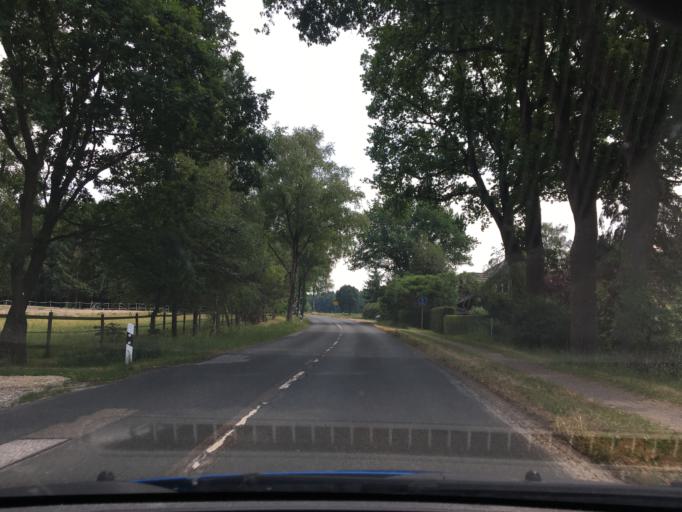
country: DE
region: Lower Saxony
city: Asendorf
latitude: 53.2671
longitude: 9.9825
